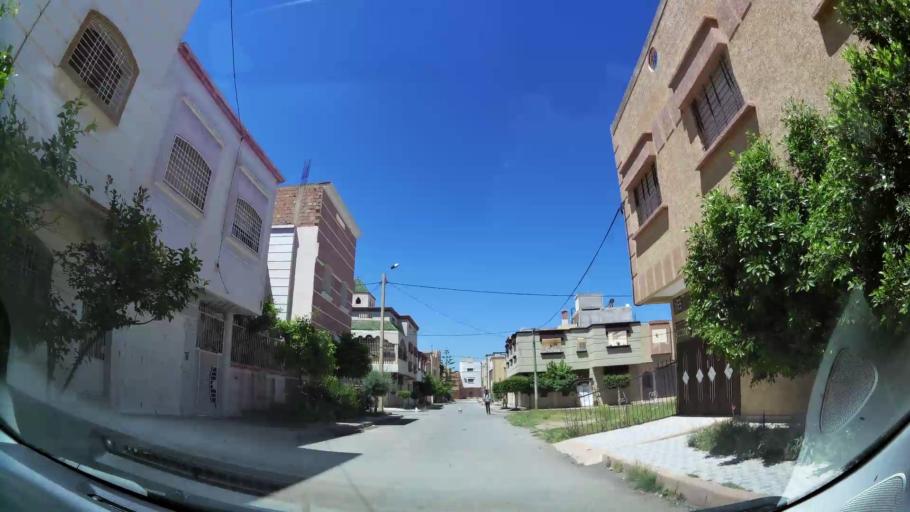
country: MA
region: Oriental
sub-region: Oujda-Angad
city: Oujda
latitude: 34.6705
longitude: -1.8850
